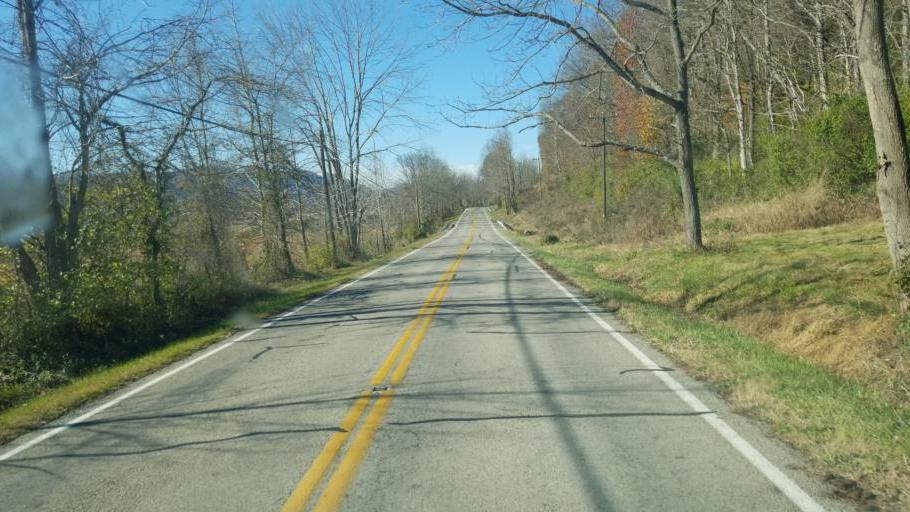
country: US
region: Kentucky
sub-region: Lewis County
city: Vanceburg
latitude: 38.6223
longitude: -83.1874
